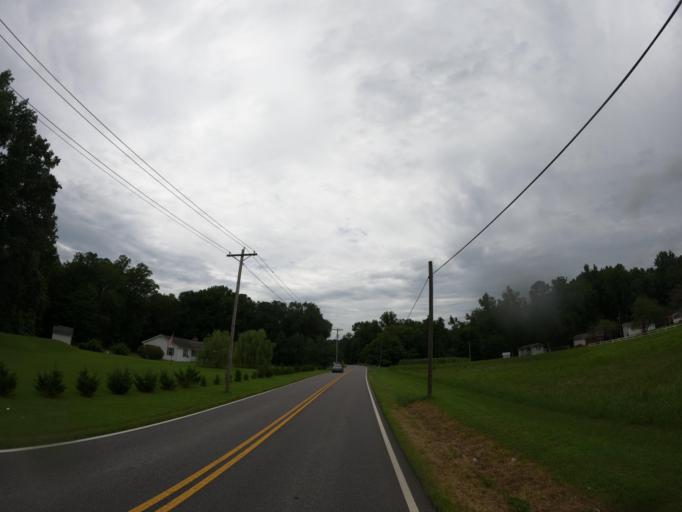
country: US
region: Maryland
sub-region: Saint Mary's County
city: California
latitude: 38.2498
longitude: -76.5068
